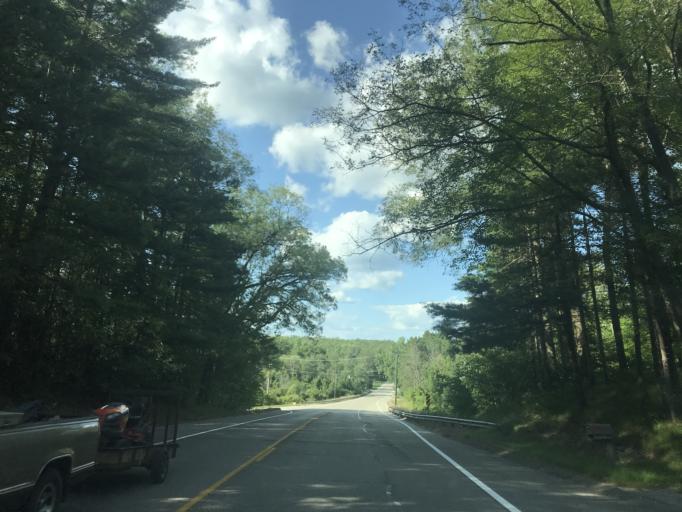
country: US
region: Michigan
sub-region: Newaygo County
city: Newaygo
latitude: 43.4516
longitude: -85.7812
